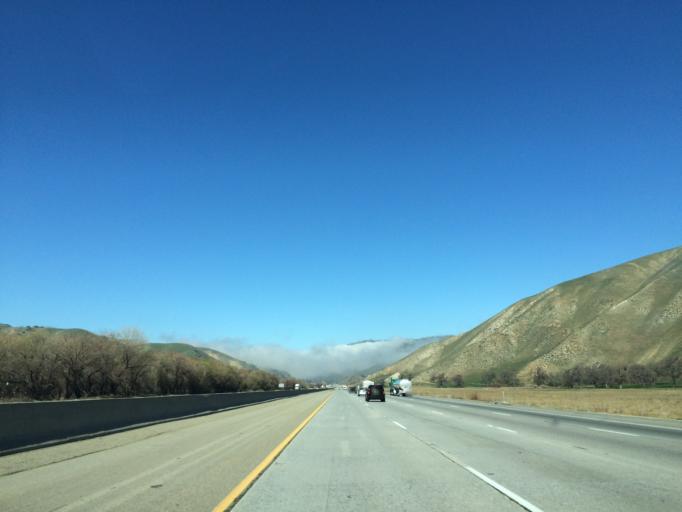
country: US
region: California
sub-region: Kern County
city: Lebec
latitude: 34.8432
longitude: -118.8657
